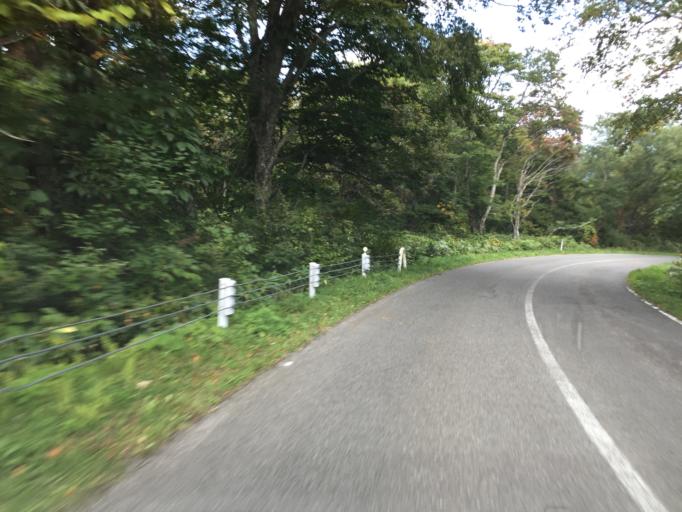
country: JP
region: Fukushima
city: Inawashiro
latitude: 37.6208
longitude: 140.0530
